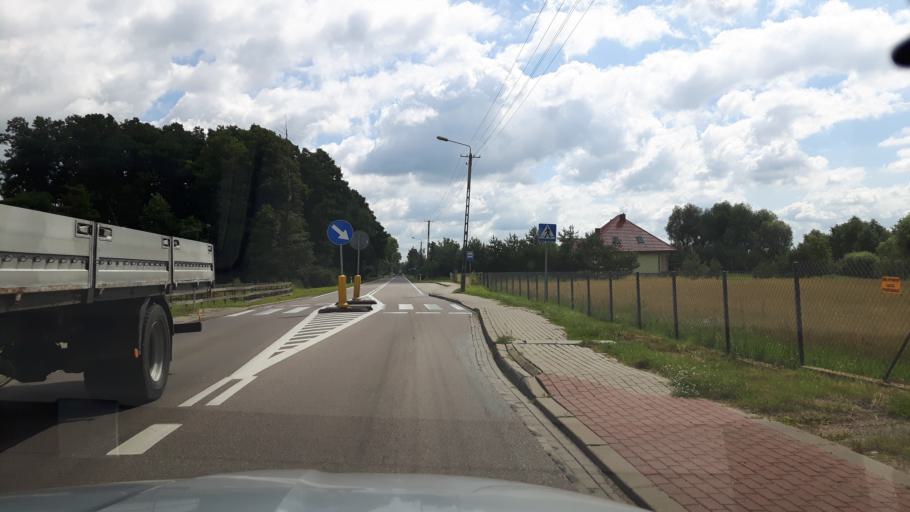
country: PL
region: Masovian Voivodeship
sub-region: Powiat ostrowski
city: Brok
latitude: 52.7044
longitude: 21.8897
